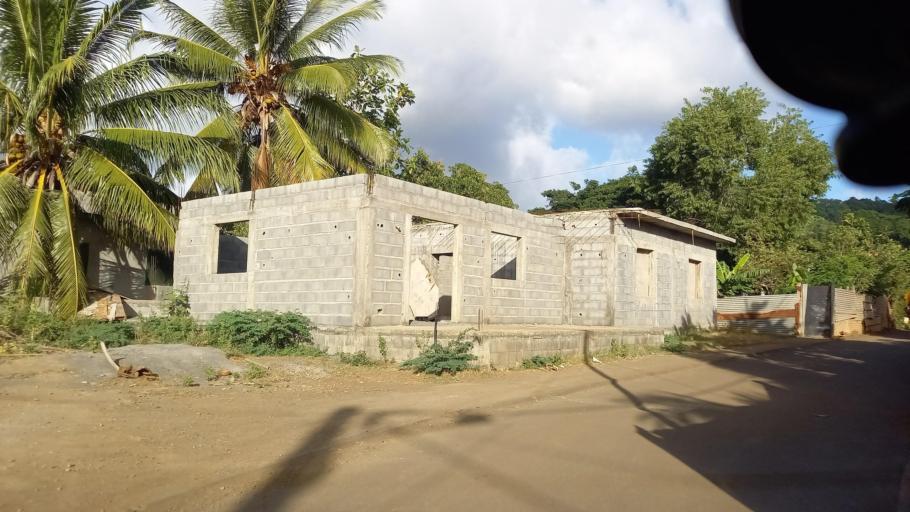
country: YT
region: Bandrele
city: Bandrele
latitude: -12.9134
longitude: 45.1944
